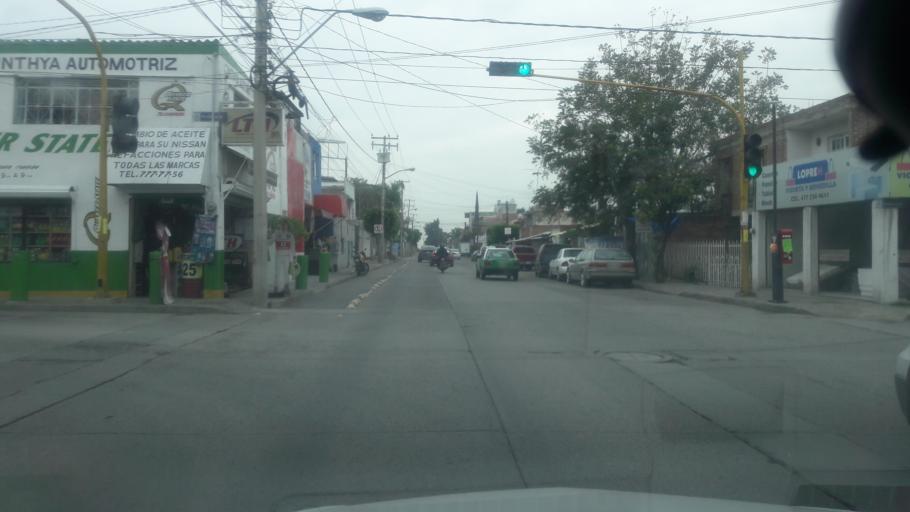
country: MX
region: Guanajuato
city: Leon
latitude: 21.1278
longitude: -101.7054
